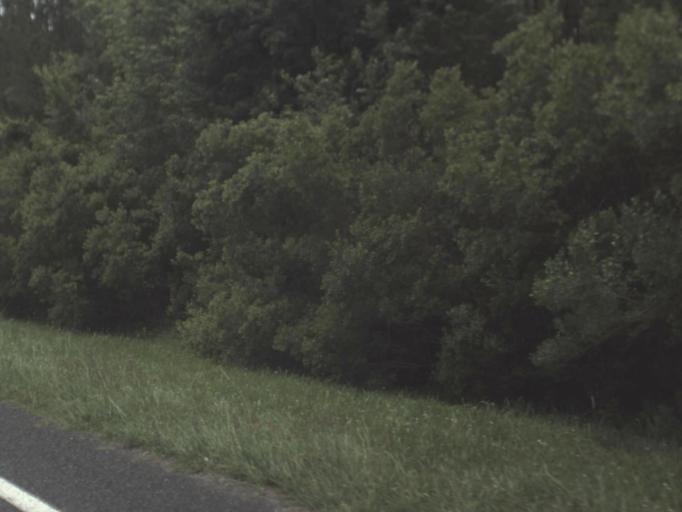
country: US
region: Florida
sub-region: Nassau County
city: Hilliard
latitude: 30.6594
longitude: -81.8807
